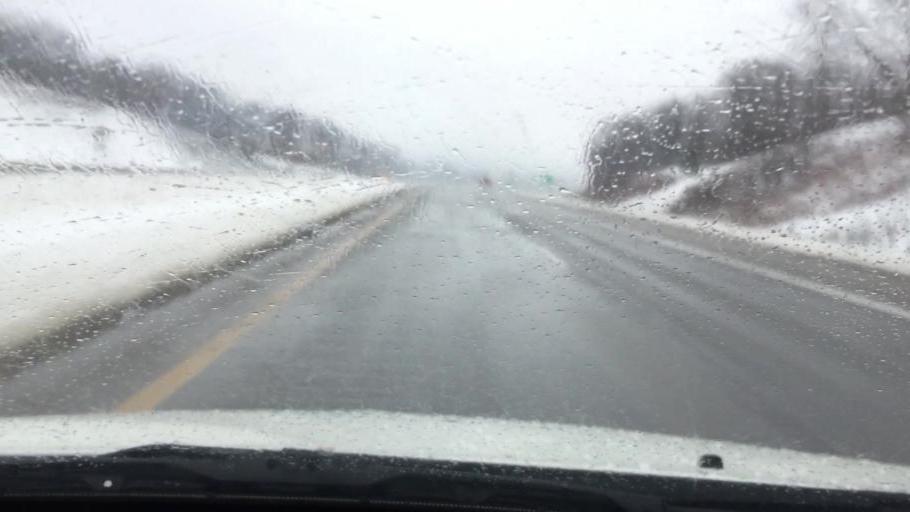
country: US
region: Michigan
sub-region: Wexford County
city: Cadillac
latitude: 44.2969
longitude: -85.3909
